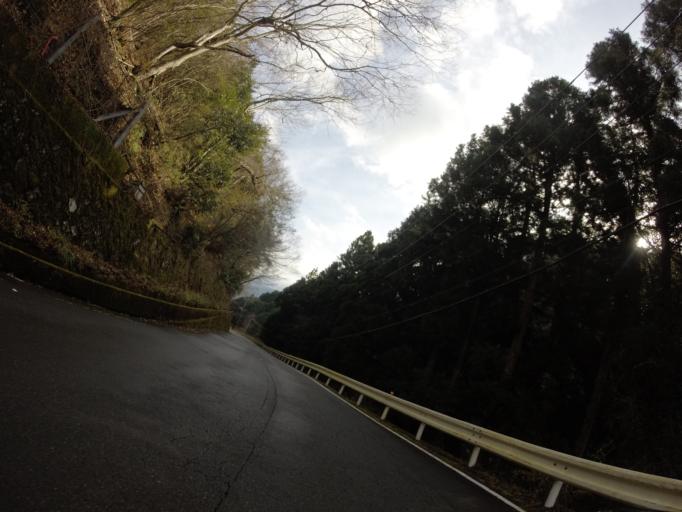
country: JP
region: Shizuoka
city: Heda
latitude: 34.8872
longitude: 138.8961
